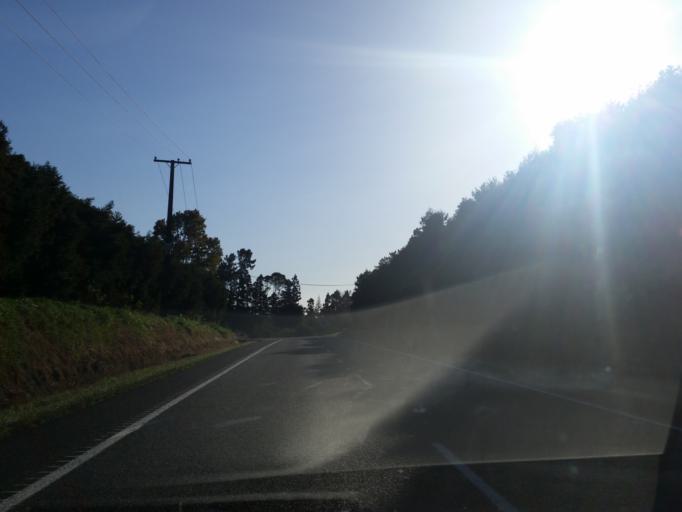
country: NZ
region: Bay of Plenty
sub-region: Western Bay of Plenty District
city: Katikati
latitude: -37.4849
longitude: 175.9304
